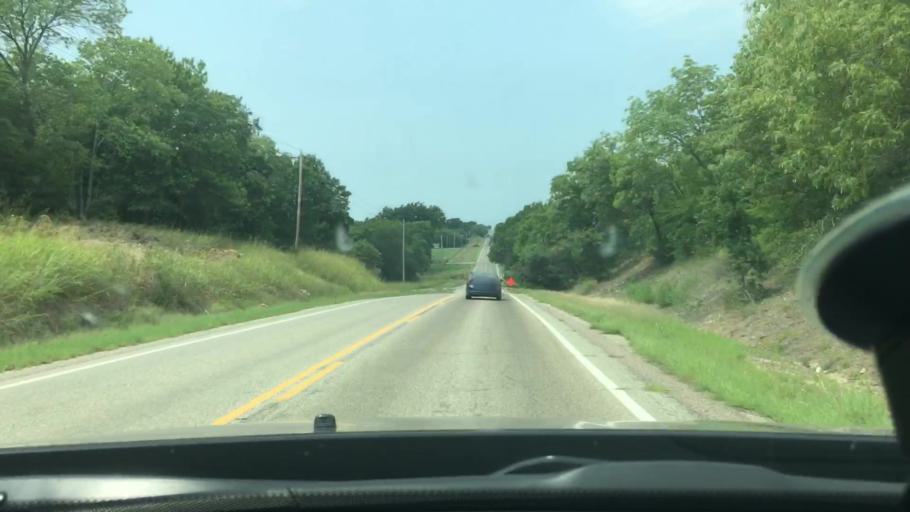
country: US
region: Oklahoma
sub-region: Marshall County
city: Kingston
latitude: 33.9983
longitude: -96.8257
